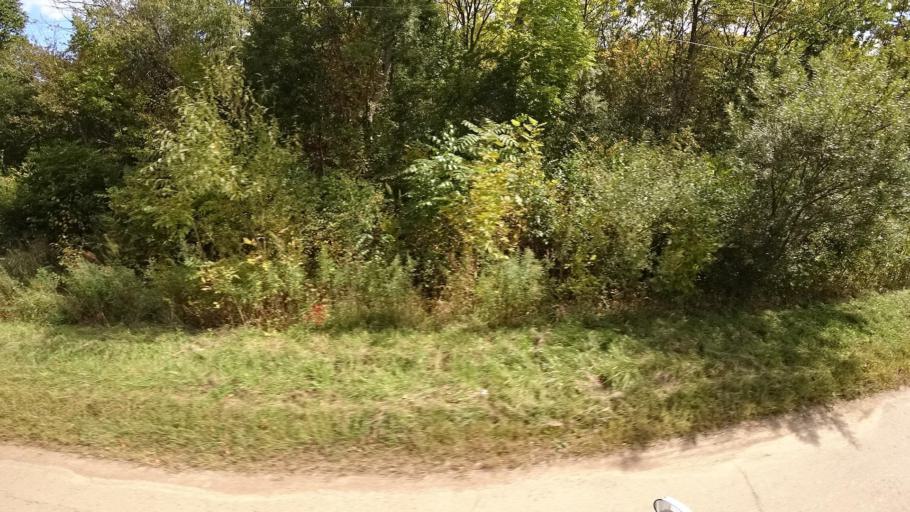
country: RU
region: Primorskiy
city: Yakovlevka
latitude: 44.7501
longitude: 133.6059
